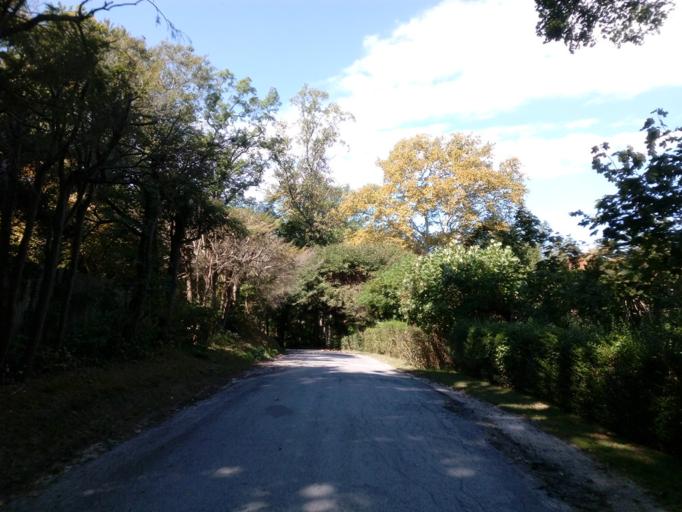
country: US
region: New York
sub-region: Nassau County
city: Laurel Hollow
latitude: 40.8710
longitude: -73.4804
